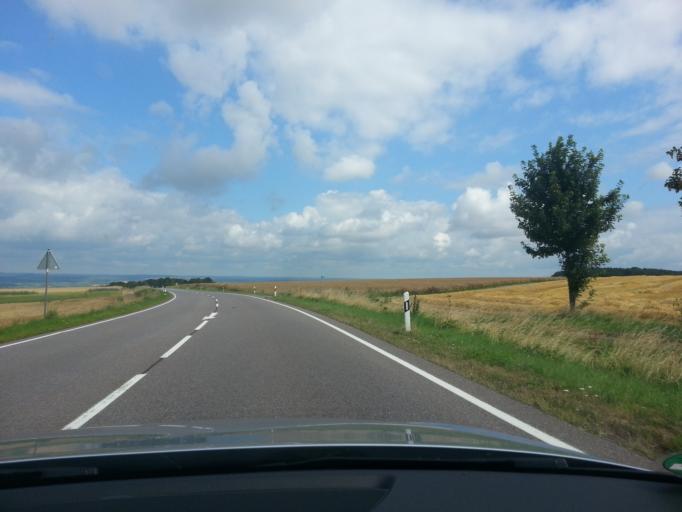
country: DE
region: Rheinland-Pfalz
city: Kirf
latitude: 49.5194
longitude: 6.4457
